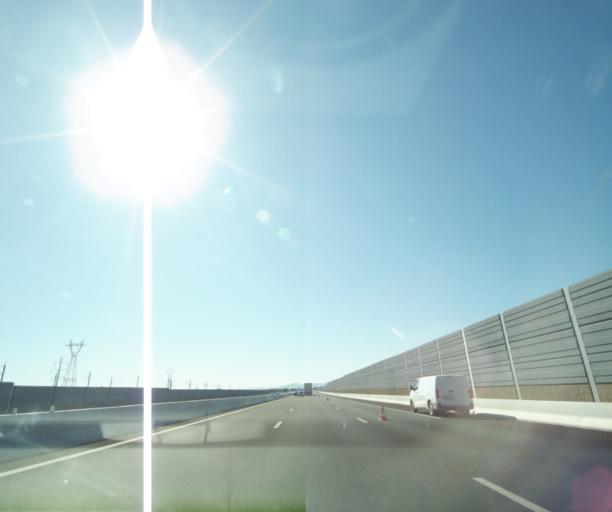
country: FR
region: Languedoc-Roussillon
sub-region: Departement de l'Herault
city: Lattes
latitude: 43.5859
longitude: 3.9019
